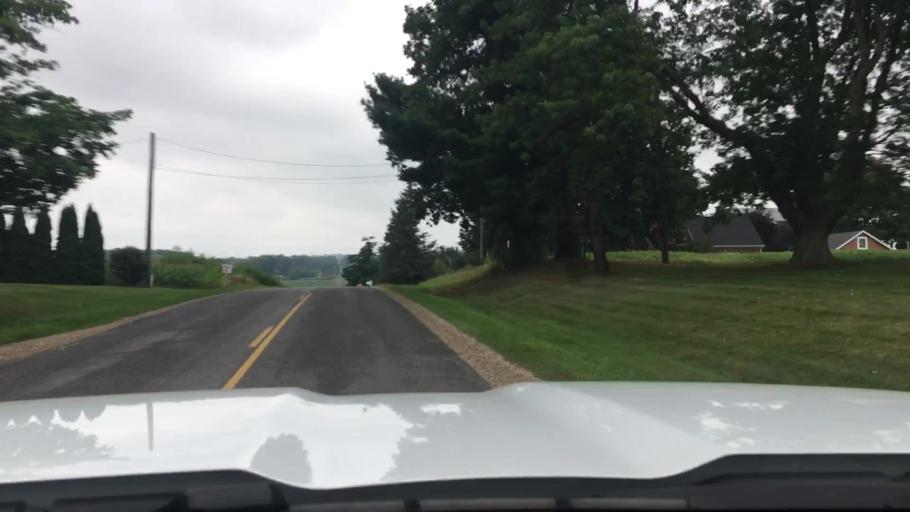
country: US
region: Michigan
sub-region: Ottawa County
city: Hudsonville
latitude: 42.7861
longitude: -85.8616
